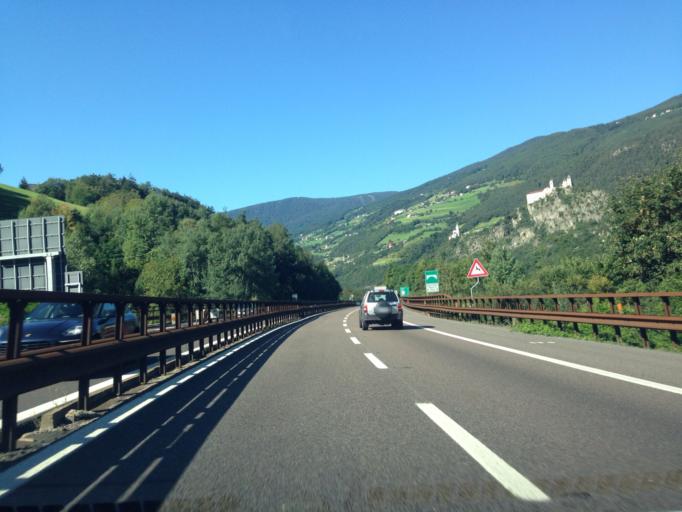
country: IT
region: Trentino-Alto Adige
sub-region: Bolzano
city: Chiusa
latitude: 46.6434
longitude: 11.5804
